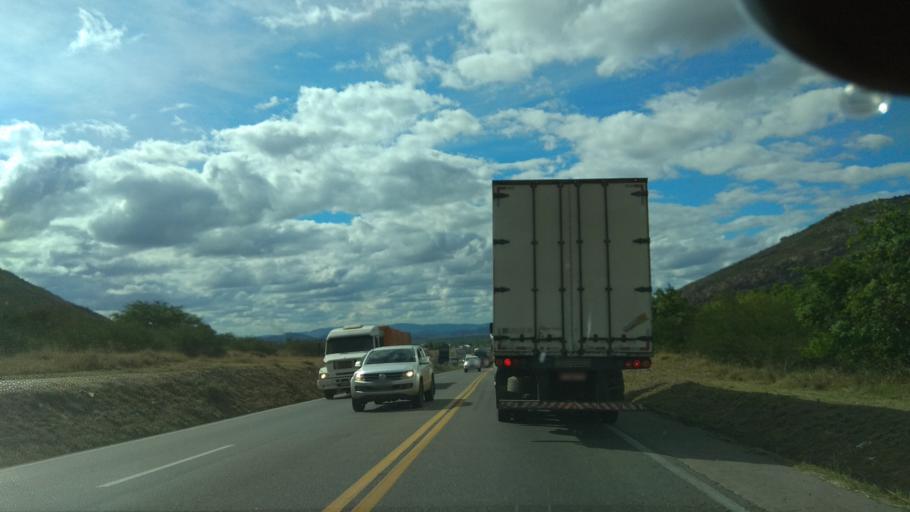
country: BR
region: Bahia
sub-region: Amargosa
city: Amargosa
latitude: -12.8820
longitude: -39.8584
